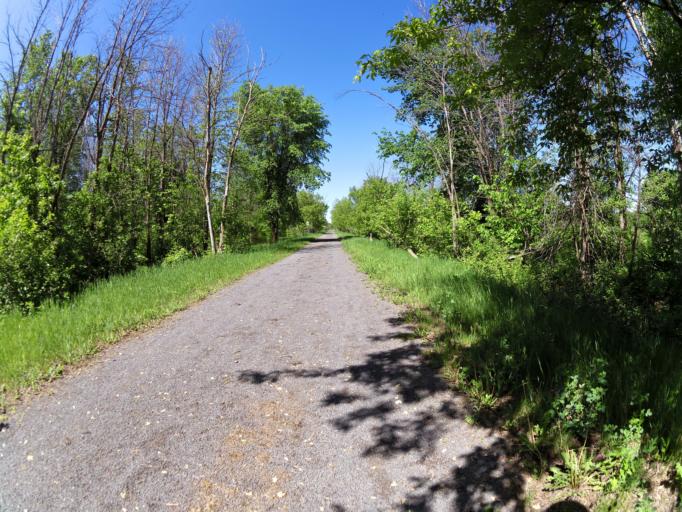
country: CA
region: Ontario
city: Clarence-Rockland
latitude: 45.4281
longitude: -75.3009
